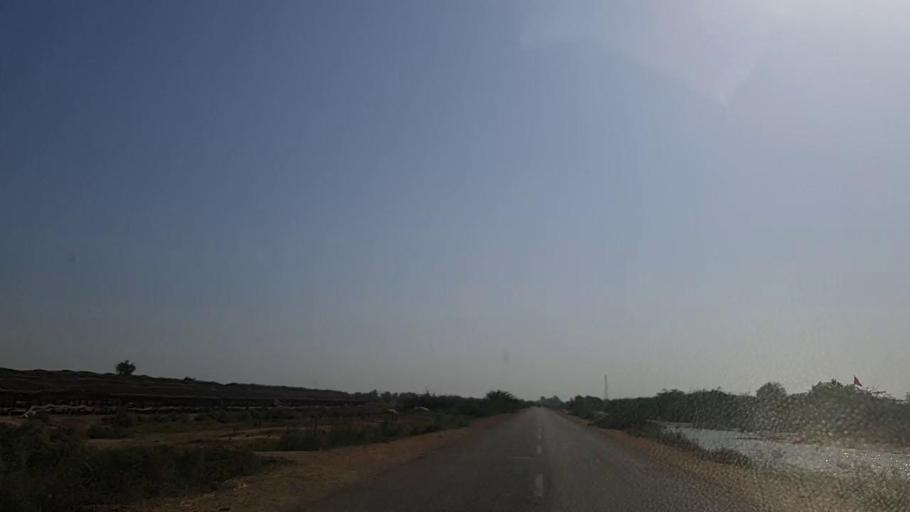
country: PK
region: Sindh
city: Jati
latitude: 24.5267
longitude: 68.2772
